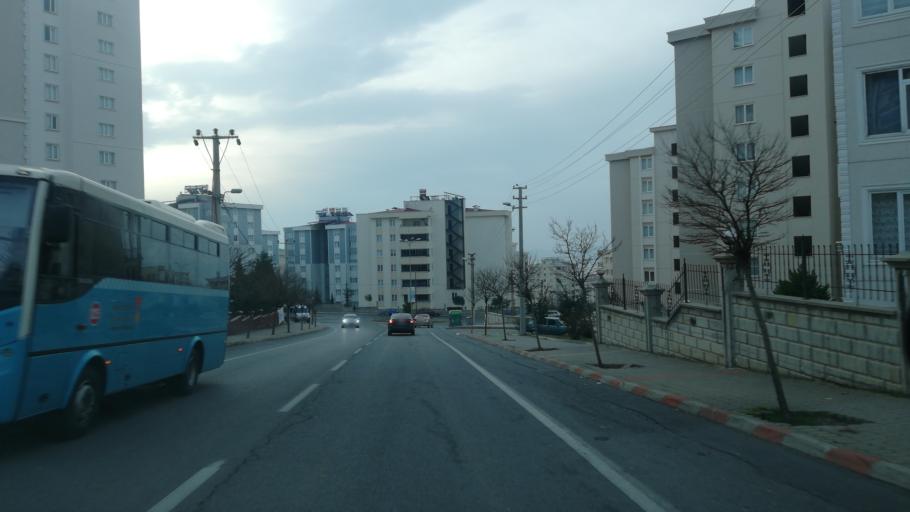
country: TR
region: Kahramanmaras
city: Kahramanmaras
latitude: 37.5983
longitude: 36.8916
